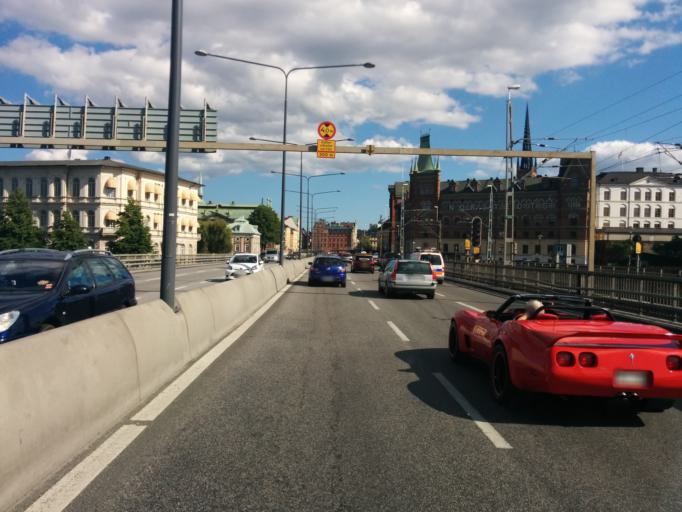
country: SE
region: Stockholm
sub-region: Stockholms Kommun
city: Stockholm
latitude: 59.3275
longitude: 18.0614
